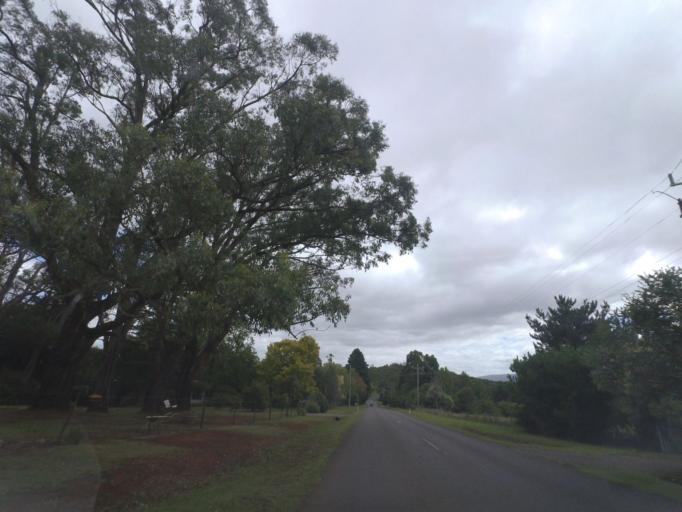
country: AU
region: Victoria
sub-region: Yarra Ranges
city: Launching Place
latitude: -37.8372
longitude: 145.5856
